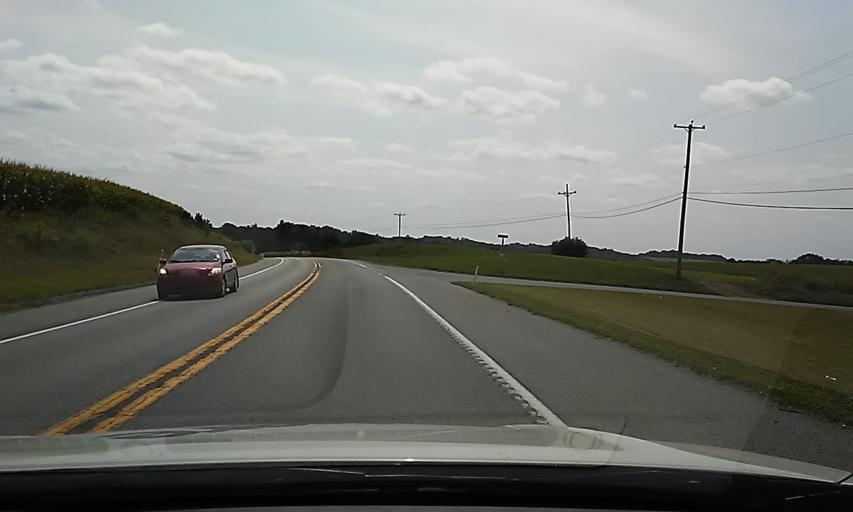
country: US
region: Pennsylvania
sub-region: Jefferson County
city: Punxsutawney
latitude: 40.8982
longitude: -79.0162
